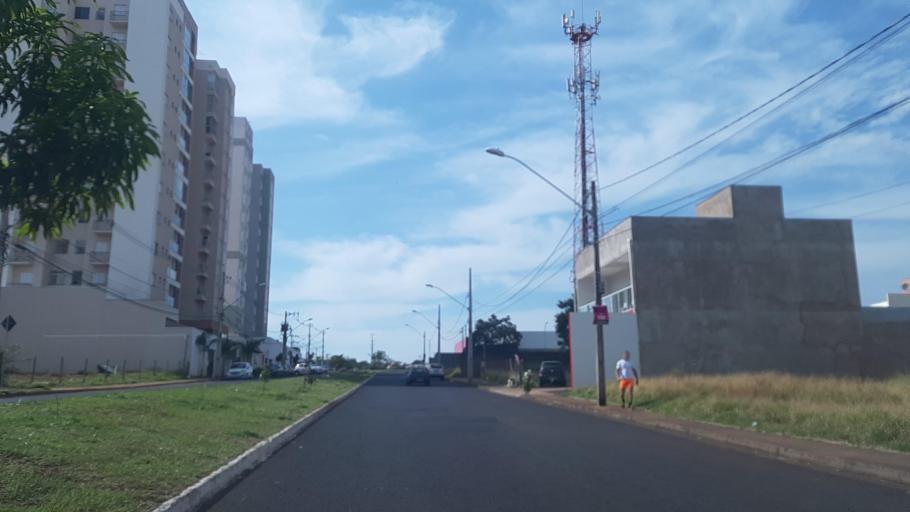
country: BR
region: Minas Gerais
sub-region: Uberlandia
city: Uberlandia
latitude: -18.8721
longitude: -48.2341
